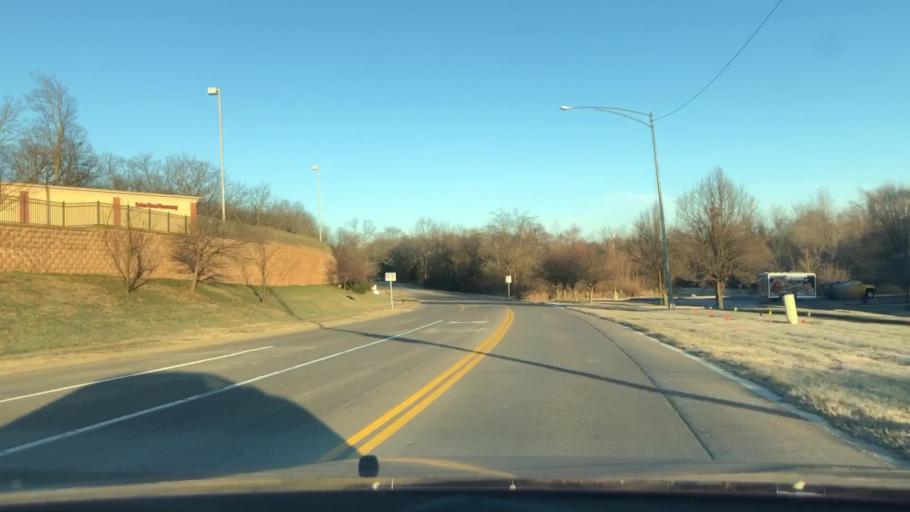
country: US
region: Missouri
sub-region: Greene County
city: Springfield
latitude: 37.1592
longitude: -93.2413
